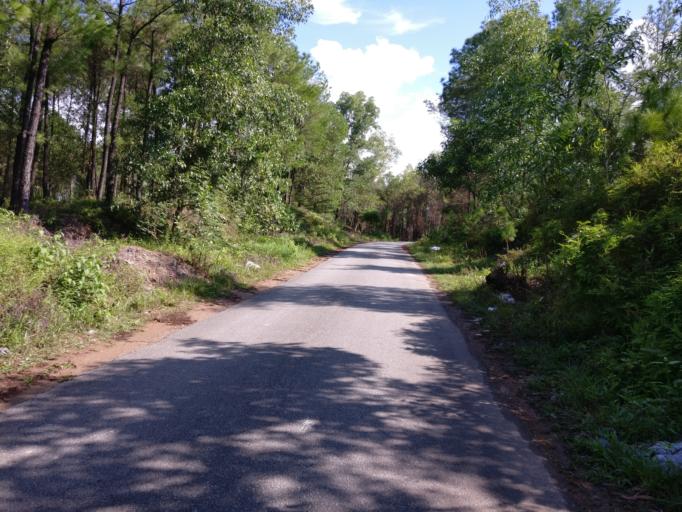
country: VN
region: Thua Thien-Hue
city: Hue
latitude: 16.4094
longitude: 107.5936
